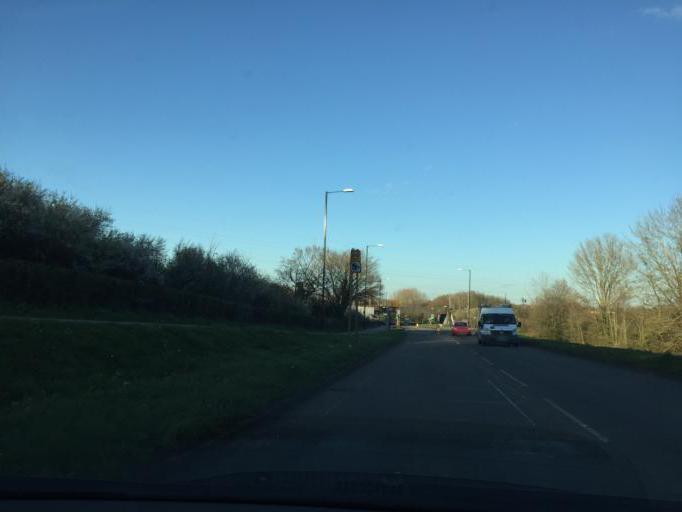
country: GB
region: England
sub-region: Coventry
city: Coventry
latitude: 52.3924
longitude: -1.4750
